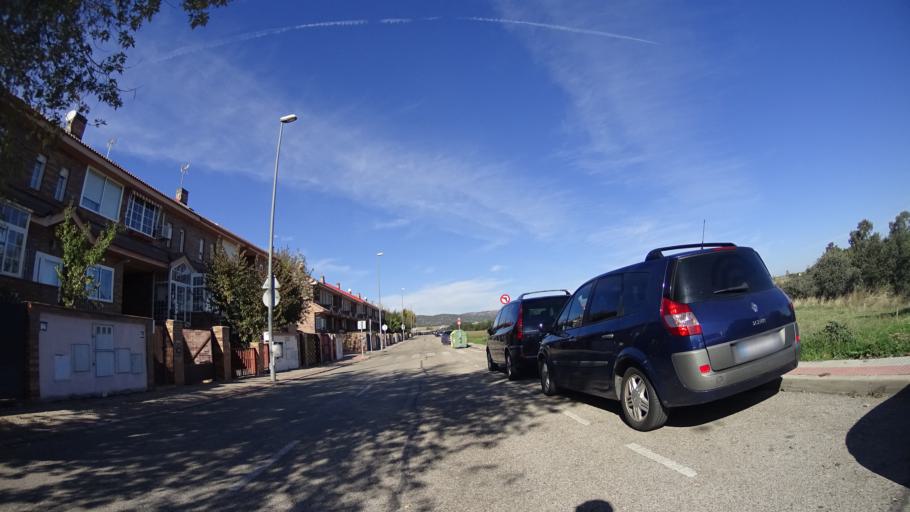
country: ES
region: Madrid
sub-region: Provincia de Madrid
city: Villanueva del Pardillo
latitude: 40.4998
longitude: -3.9653
